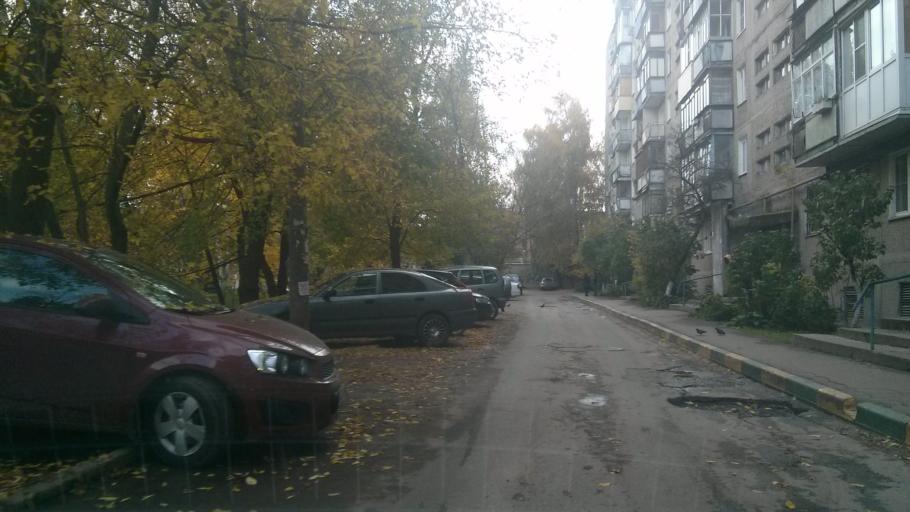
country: RU
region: Nizjnij Novgorod
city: Nizhniy Novgorod
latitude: 56.3029
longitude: 44.0367
